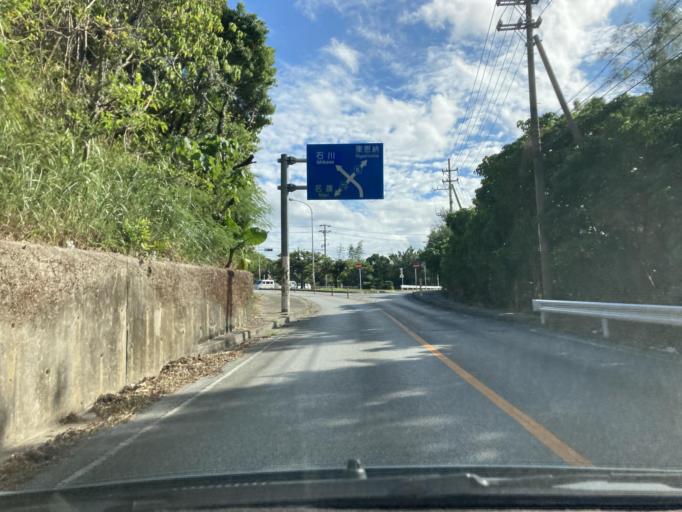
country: JP
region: Okinawa
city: Ishikawa
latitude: 26.4350
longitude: 127.8072
